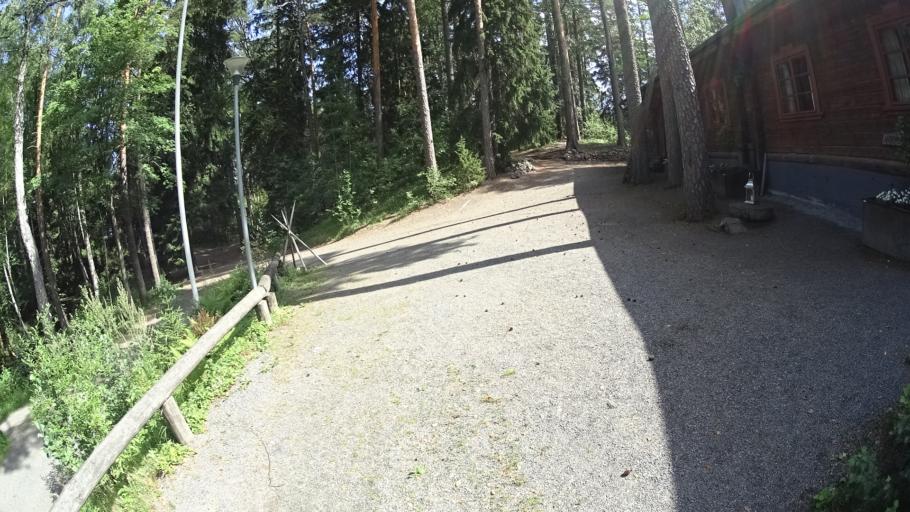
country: FI
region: Haeme
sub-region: Forssa
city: Tammela
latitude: 60.7761
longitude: 23.8466
